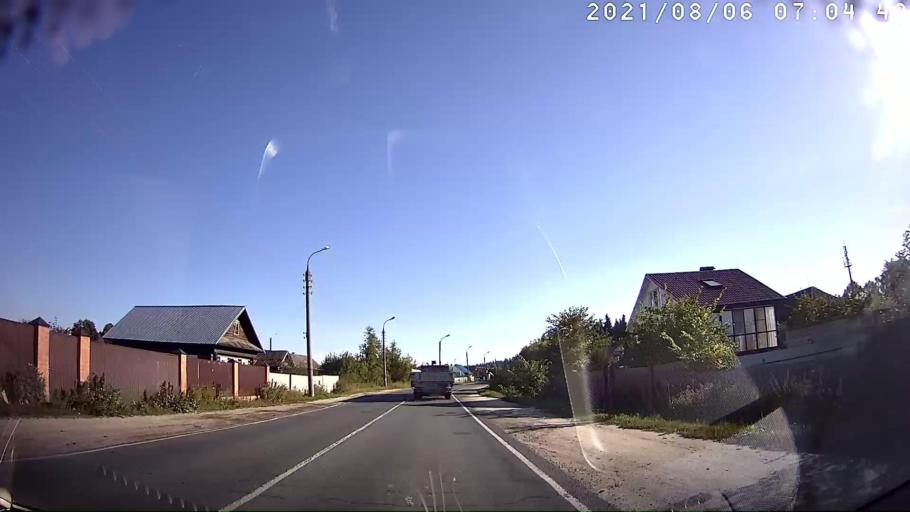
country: RU
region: Mariy-El
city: Yoshkar-Ola
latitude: 56.5497
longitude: 47.9837
